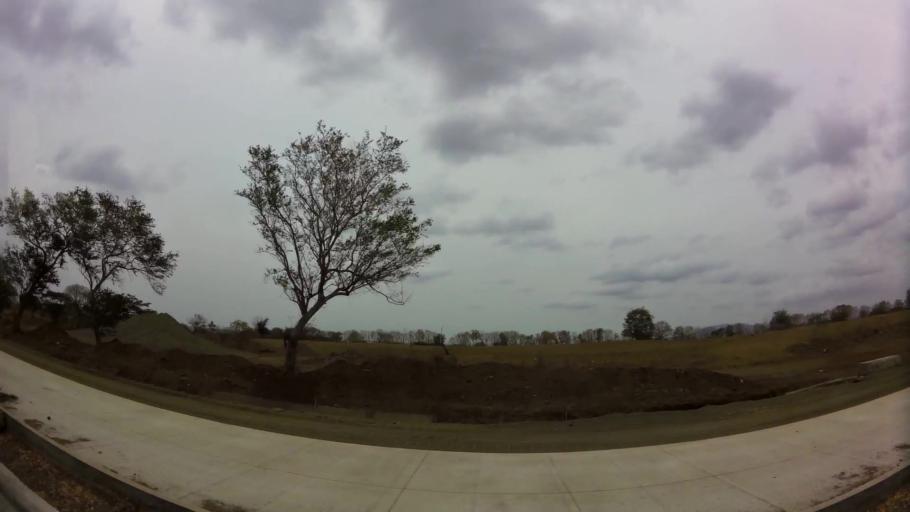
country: NI
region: Masaya
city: Ticuantepe
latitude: 12.0905
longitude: -86.1831
